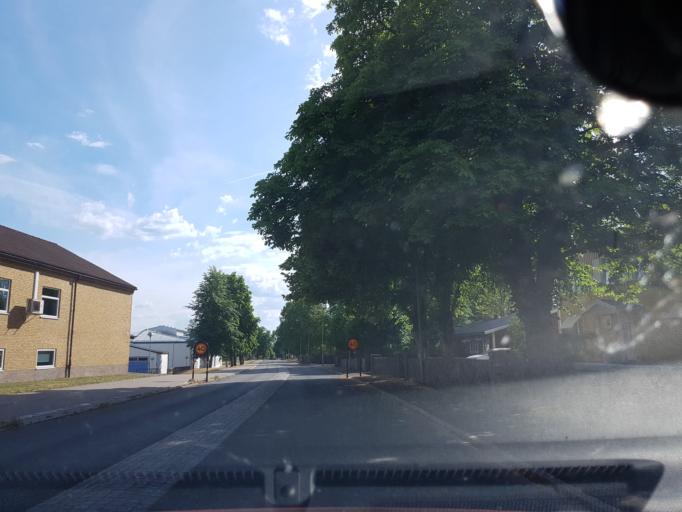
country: SE
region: Joenkoeping
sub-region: Gislaveds Kommun
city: Gislaved
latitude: 57.2979
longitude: 13.5297
